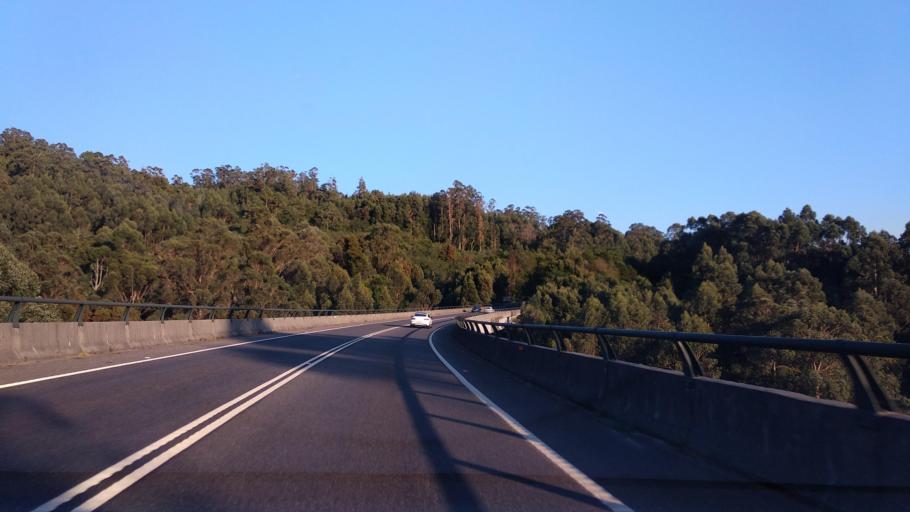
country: ES
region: Galicia
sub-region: Provincia de Pontevedra
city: Moana
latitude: 42.2886
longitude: -8.7719
